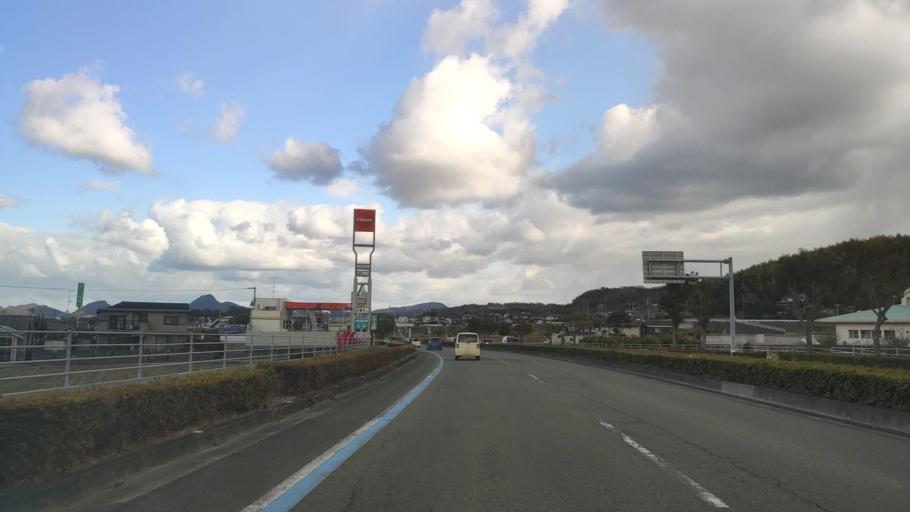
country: JP
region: Ehime
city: Hojo
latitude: 33.9362
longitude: 132.7718
